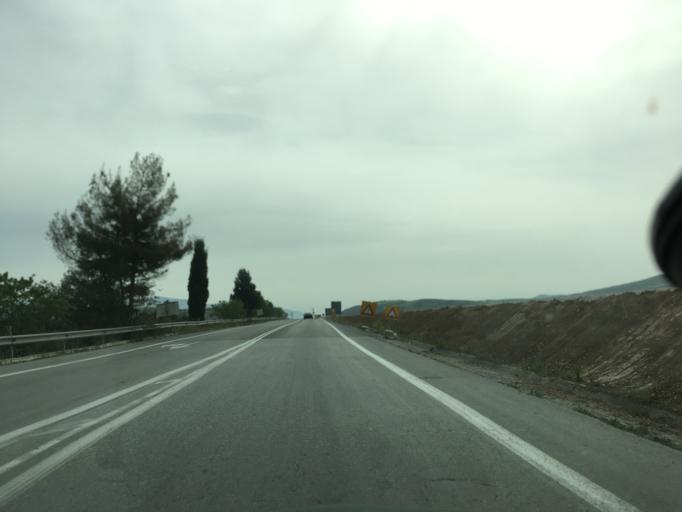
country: GR
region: Thessaly
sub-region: Nomos Magnisias
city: Velestino
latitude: 39.3869
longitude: 22.7864
